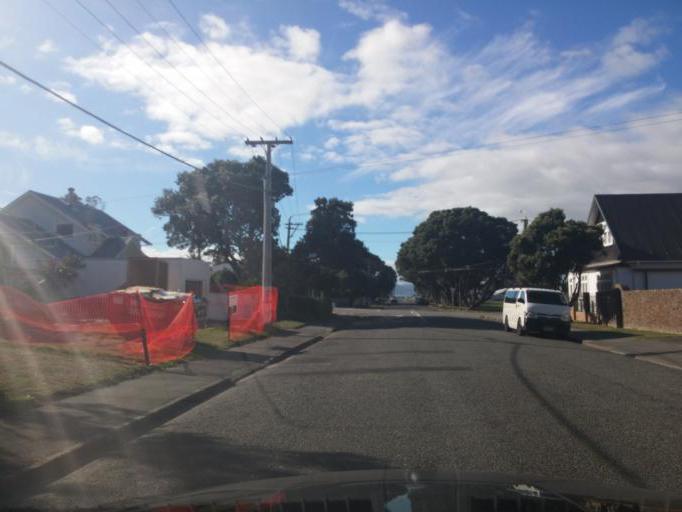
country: NZ
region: Wellington
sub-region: Wellington City
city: Wellington
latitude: -41.3265
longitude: 174.8328
